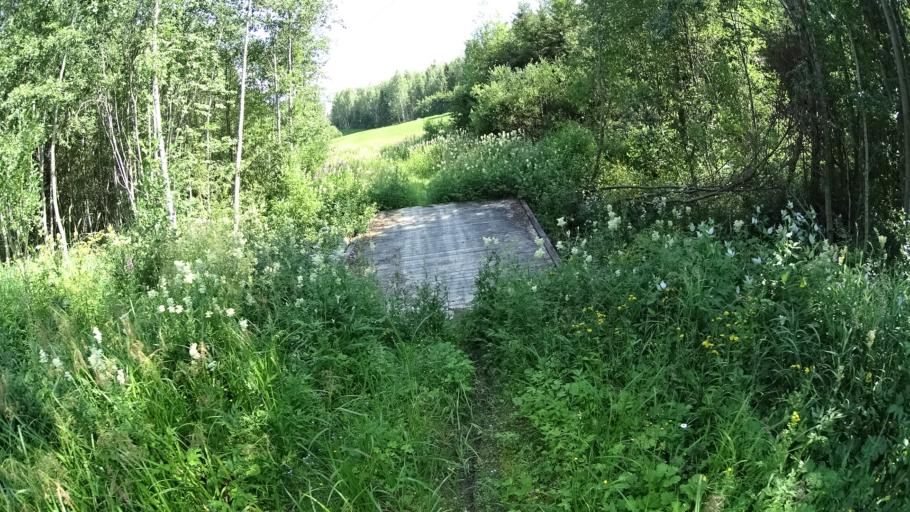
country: FI
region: North Karelia
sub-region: Pielisen Karjala
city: Lieksa
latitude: 63.1167
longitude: 29.7914
